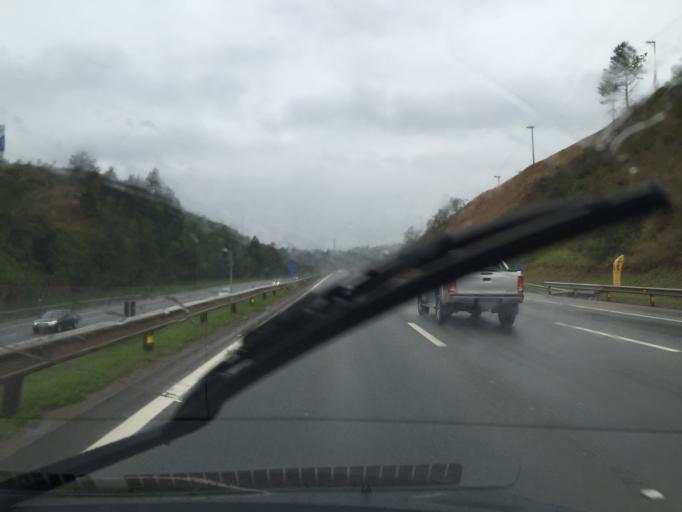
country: BR
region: Sao Paulo
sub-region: Sao Roque
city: Sao Roque
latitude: -23.4230
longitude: -47.1541
